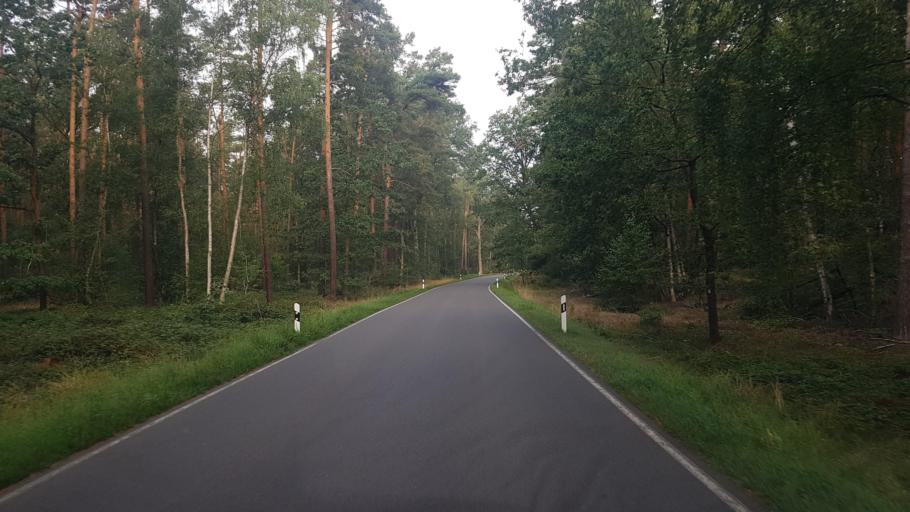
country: DE
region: Saxony-Anhalt
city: Pretzsch
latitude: 51.7590
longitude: 12.8459
